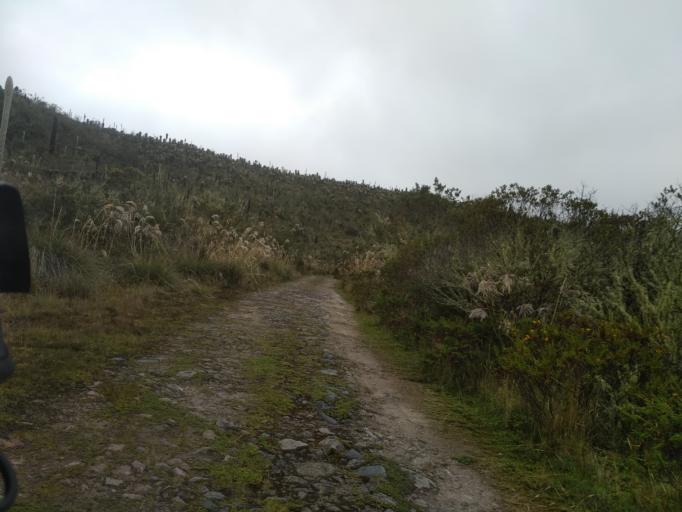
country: EC
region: Carchi
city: San Gabriel
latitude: 0.7070
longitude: -77.8271
